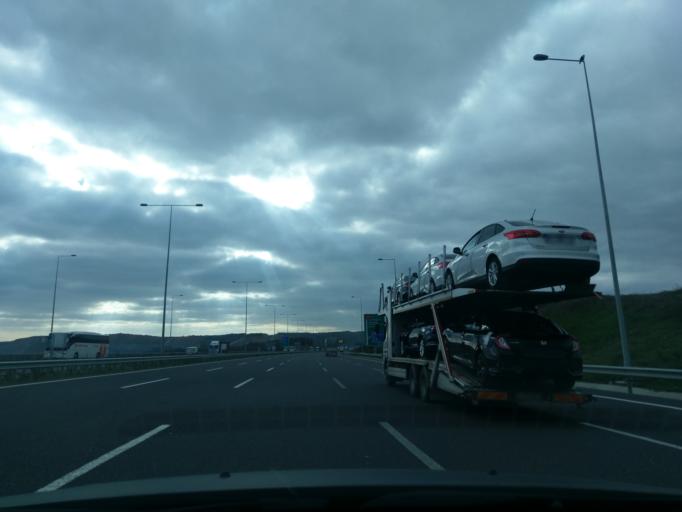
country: TR
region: Istanbul
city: Kemerburgaz
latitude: 41.2244
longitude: 28.8410
